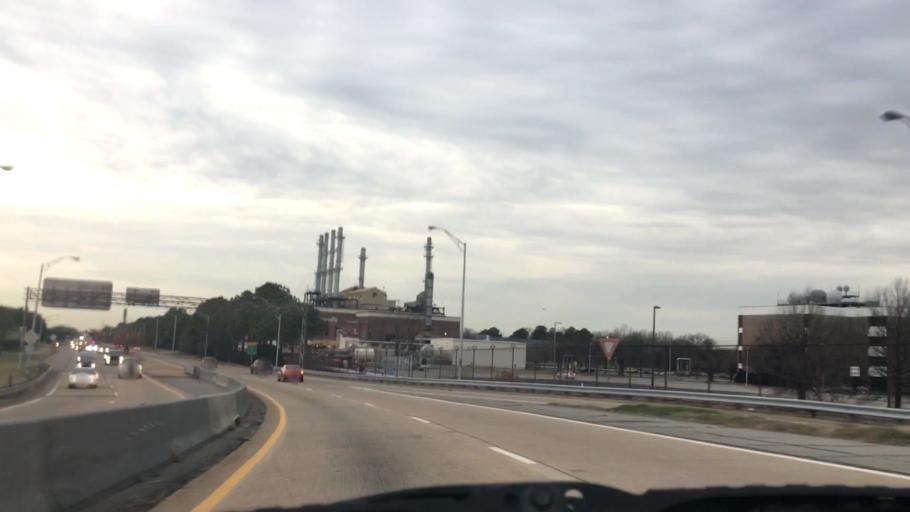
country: US
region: Virginia
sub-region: City of Hampton
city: Hampton
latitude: 36.9444
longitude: -76.3081
